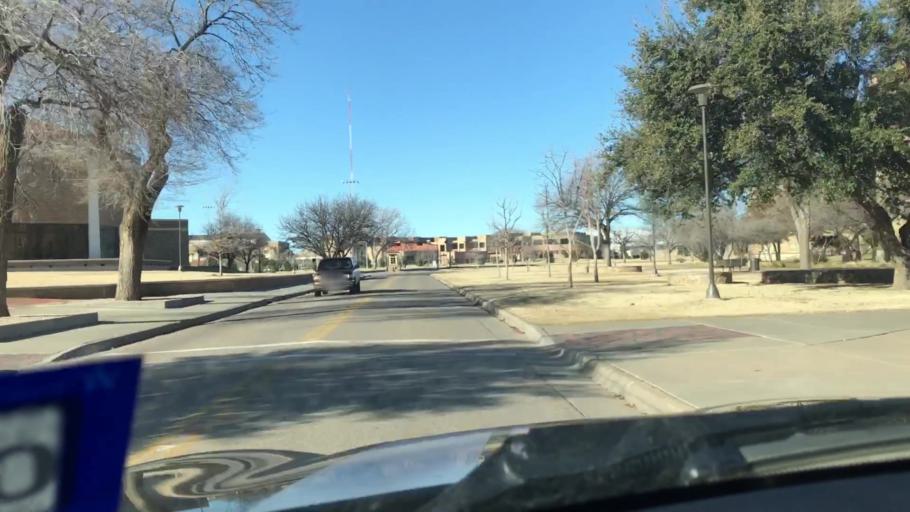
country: US
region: Texas
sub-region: Lubbock County
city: Lubbock
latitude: 33.5827
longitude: -101.8797
